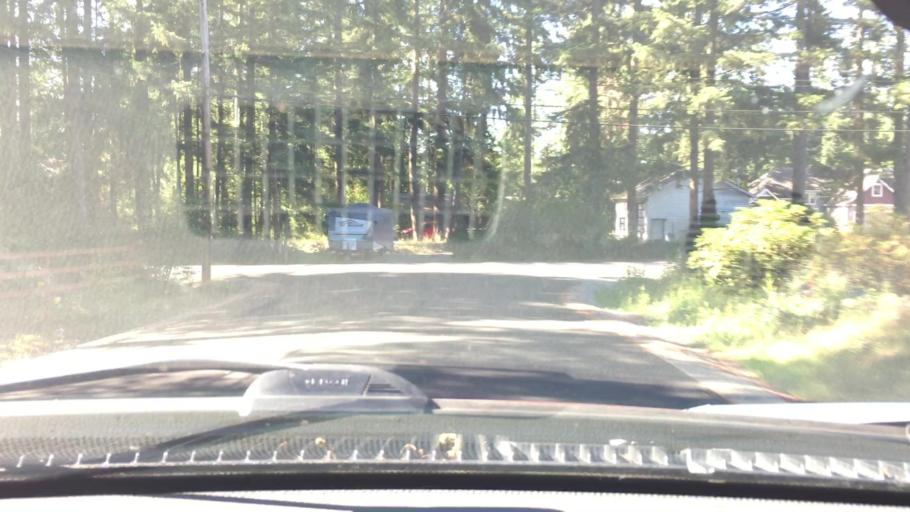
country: US
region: Washington
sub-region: King County
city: Lake Morton-Berrydale
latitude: 47.3178
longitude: -122.0993
